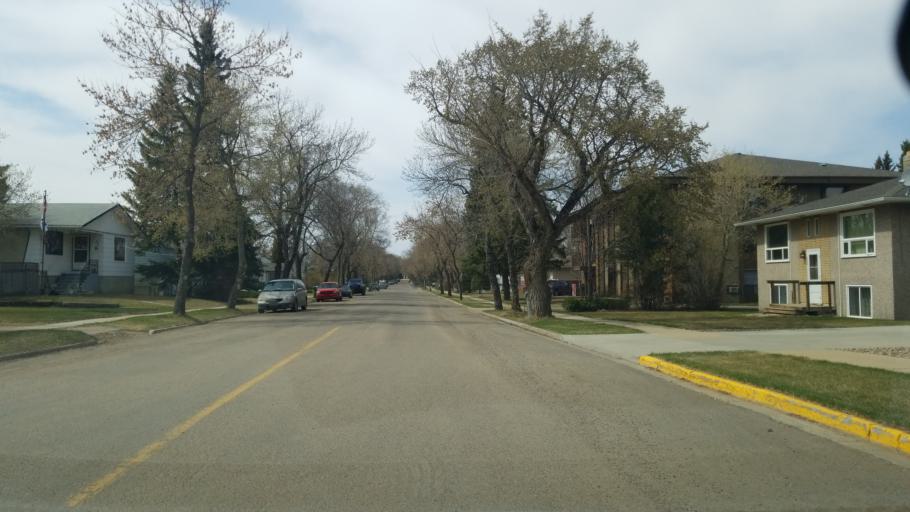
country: CA
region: Saskatchewan
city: Lloydminster
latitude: 53.2825
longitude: -110.0105
